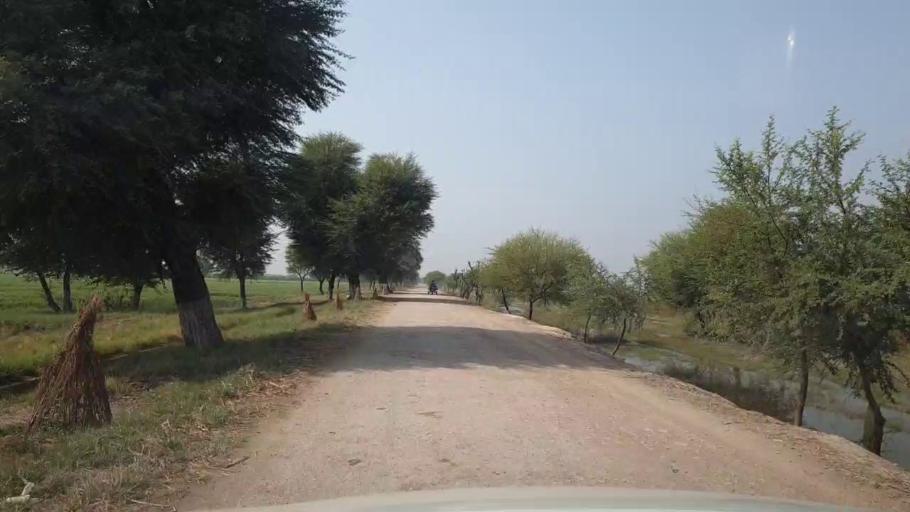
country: PK
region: Sindh
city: Umarkot
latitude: 25.4317
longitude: 69.7125
